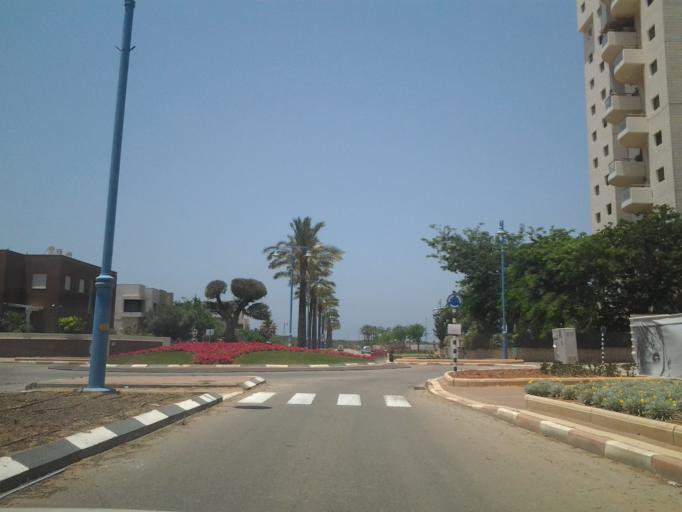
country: IL
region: Haifa
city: Hadera
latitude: 32.4290
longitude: 34.8838
